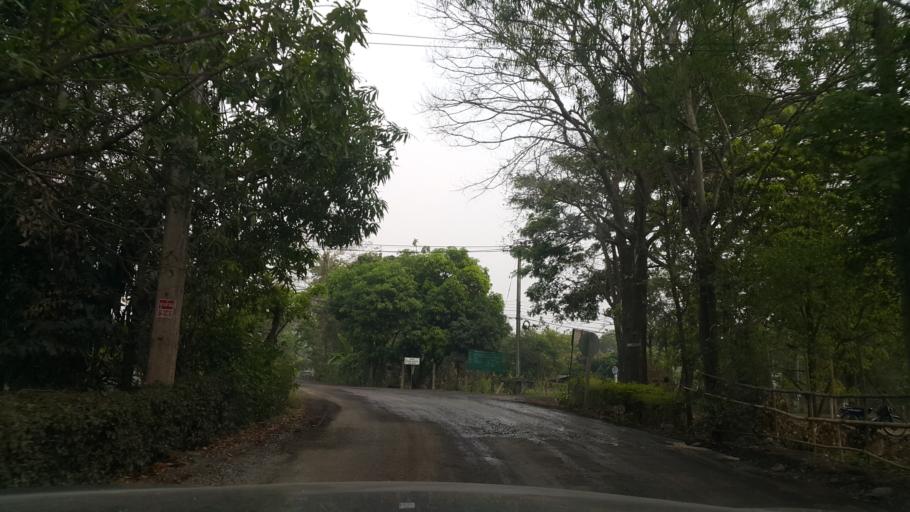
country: TH
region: Chiang Mai
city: Mae On
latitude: 18.8352
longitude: 99.2081
